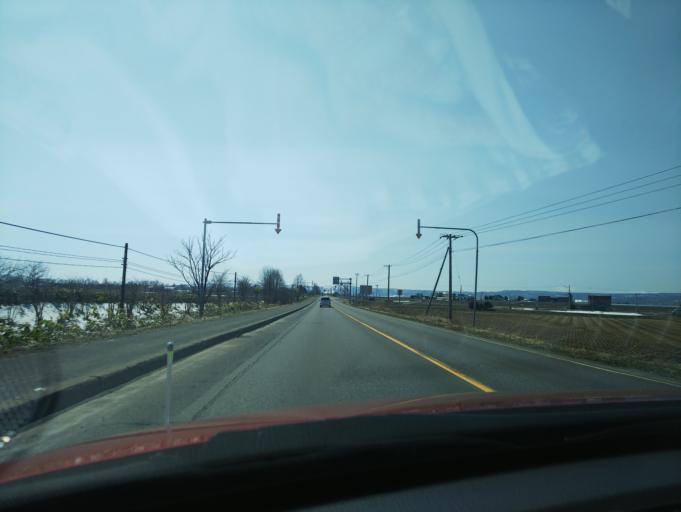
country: JP
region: Hokkaido
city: Nayoro
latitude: 44.3126
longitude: 142.4528
